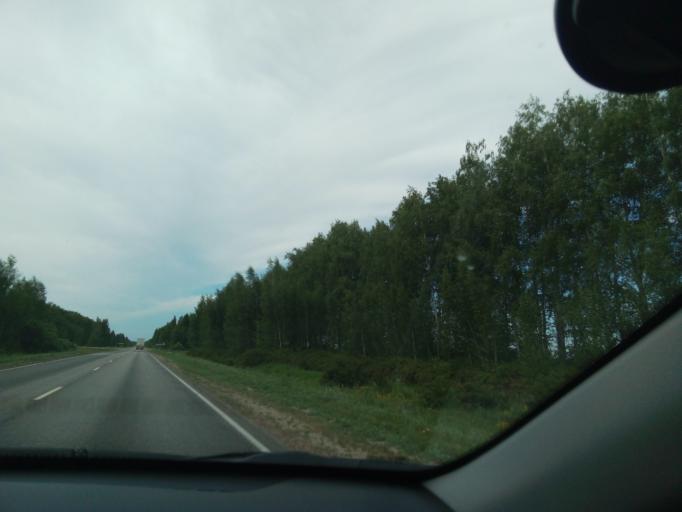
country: RU
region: Tambov
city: Zavoronezhskoye
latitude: 52.6228
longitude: 40.8486
